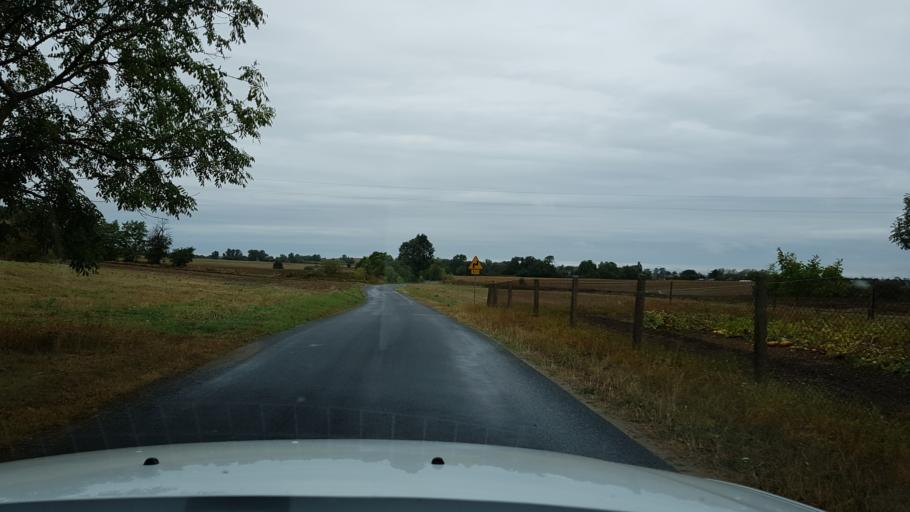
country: PL
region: West Pomeranian Voivodeship
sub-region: Powiat gryfinski
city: Cedynia
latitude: 52.8545
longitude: 14.2905
